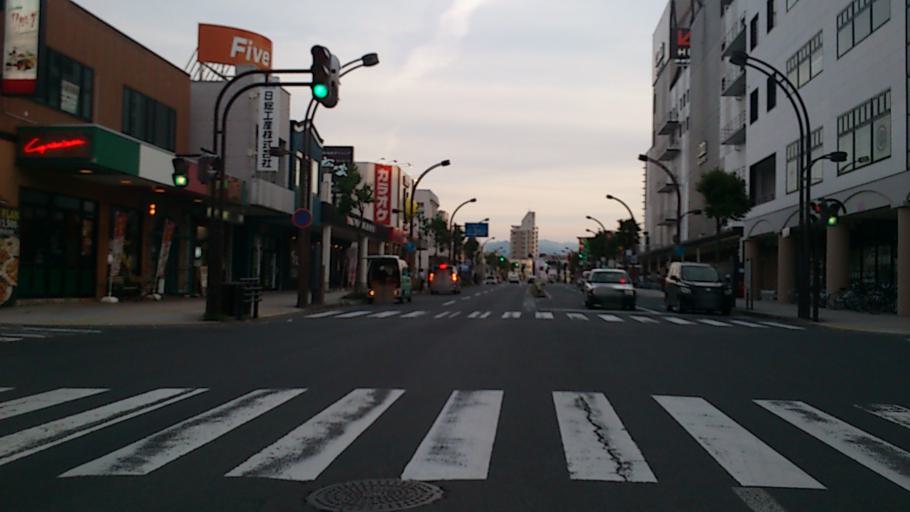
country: JP
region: Aomori
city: Hirosaki
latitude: 40.5977
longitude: 140.4831
